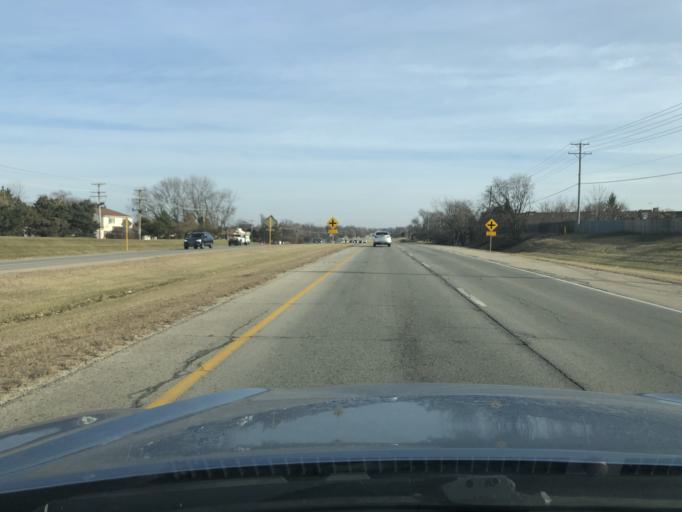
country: US
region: Illinois
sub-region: Cook County
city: South Barrington
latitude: 42.0547
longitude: -88.1278
